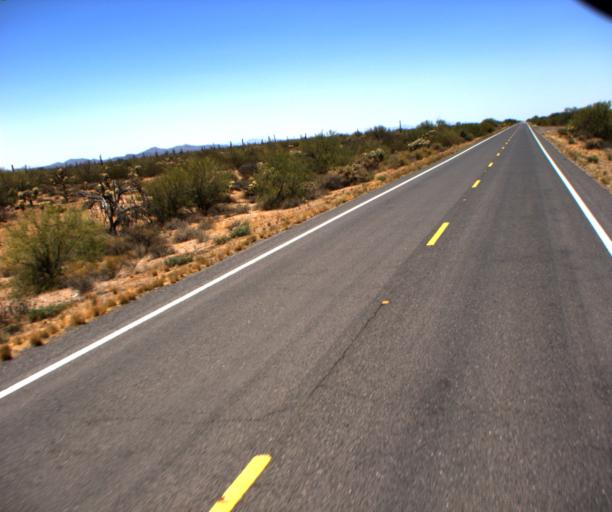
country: US
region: Arizona
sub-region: Pinal County
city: Florence
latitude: 32.7955
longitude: -111.1780
